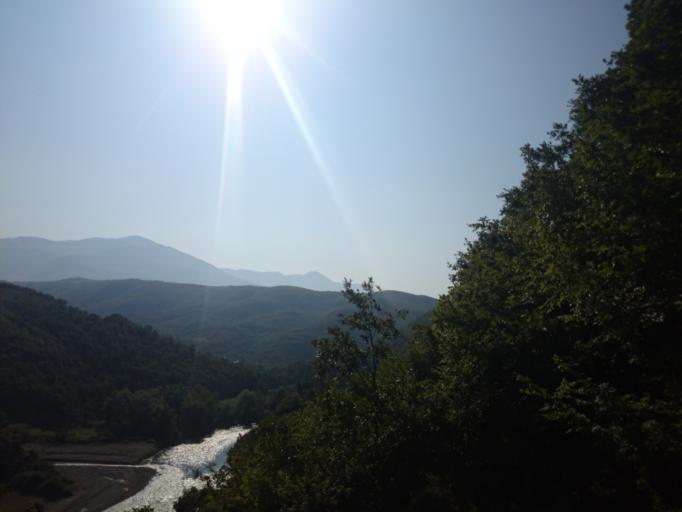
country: AL
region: Diber
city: Peshkopi
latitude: 41.6422
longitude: 20.3991
